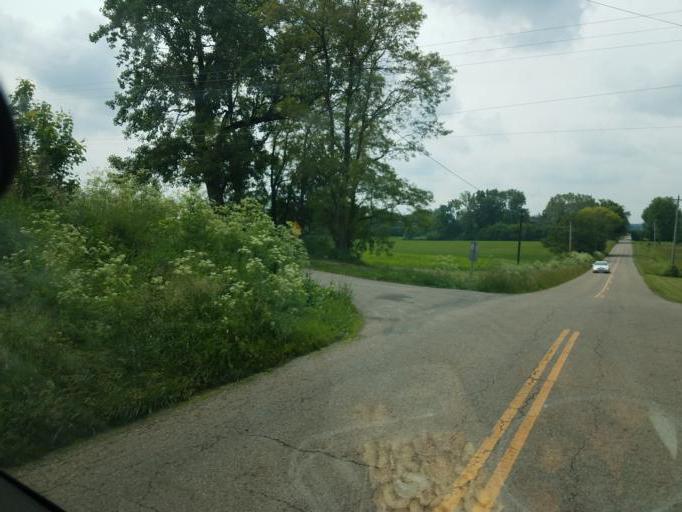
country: US
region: Ohio
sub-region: Knox County
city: Fredericktown
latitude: 40.4673
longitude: -82.5540
